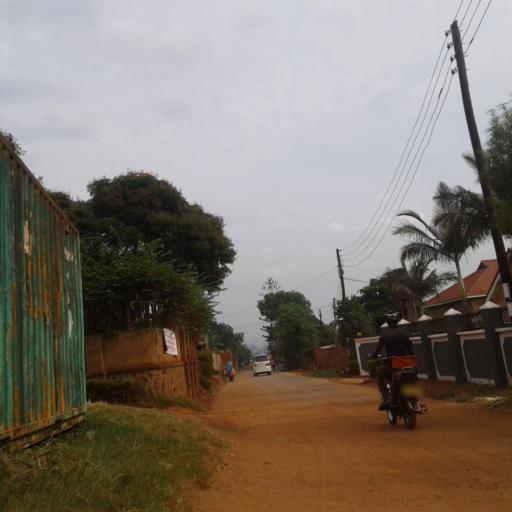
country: UG
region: Central Region
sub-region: Kampala District
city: Kampala
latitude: 0.2707
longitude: 32.6267
